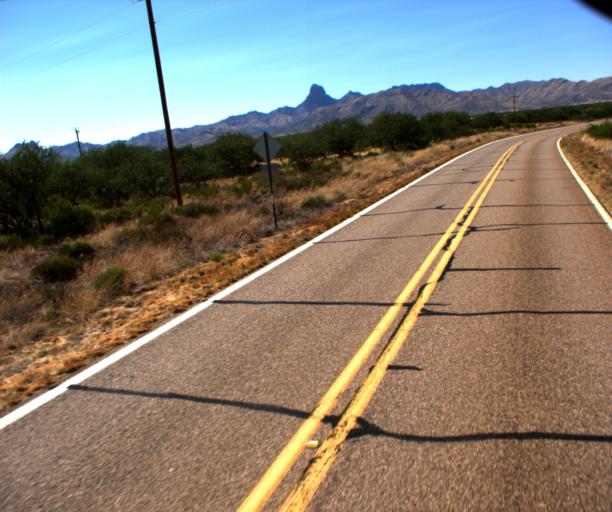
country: US
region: Arizona
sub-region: Pima County
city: Arivaca Junction
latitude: 31.6849
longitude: -111.4870
